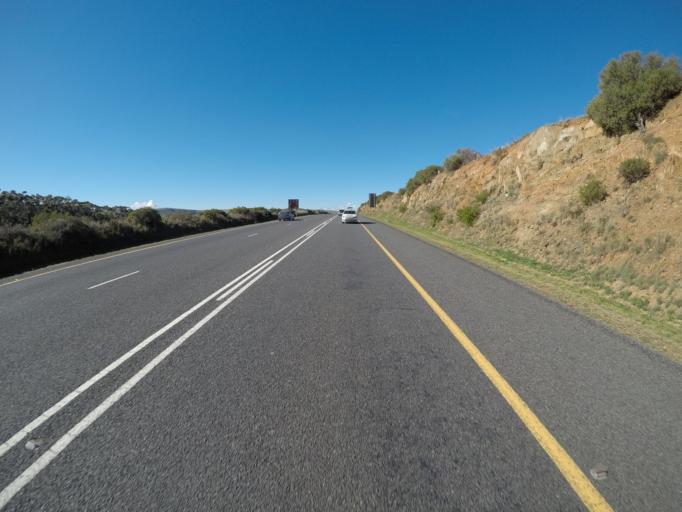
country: ZA
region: Western Cape
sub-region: Overberg District Municipality
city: Hermanus
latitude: -34.2351
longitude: 19.2220
